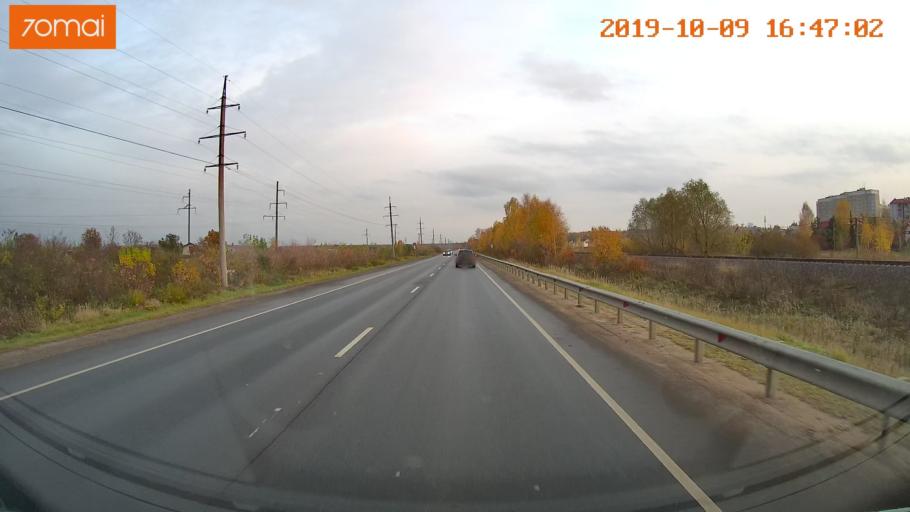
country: RU
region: Kostroma
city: Volgorechensk
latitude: 57.4395
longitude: 41.1719
